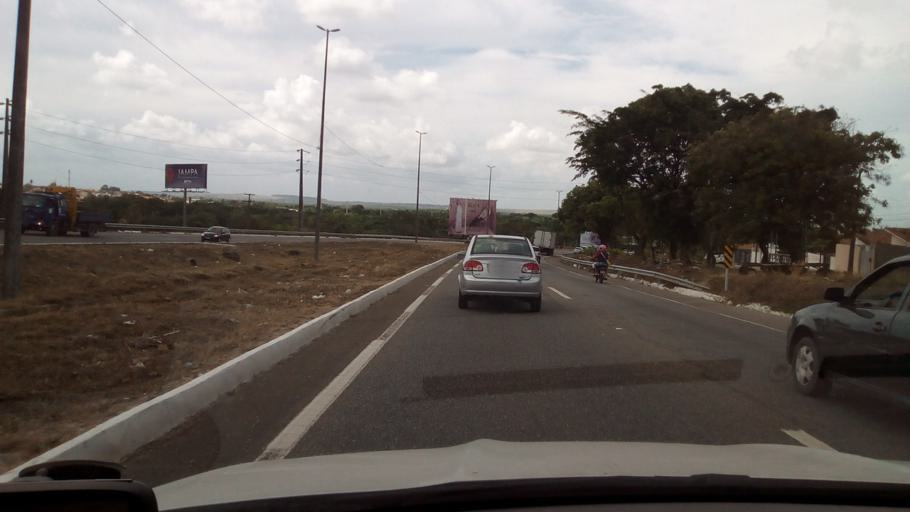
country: BR
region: Paraiba
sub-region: Joao Pessoa
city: Joao Pessoa
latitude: -7.1029
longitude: -34.8465
